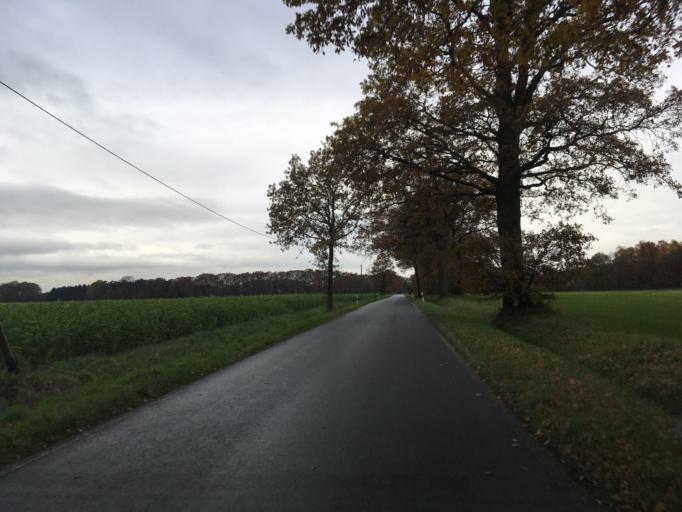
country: DE
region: North Rhine-Westphalia
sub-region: Regierungsbezirk Munster
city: Gescher
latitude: 51.9776
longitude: 7.0015
